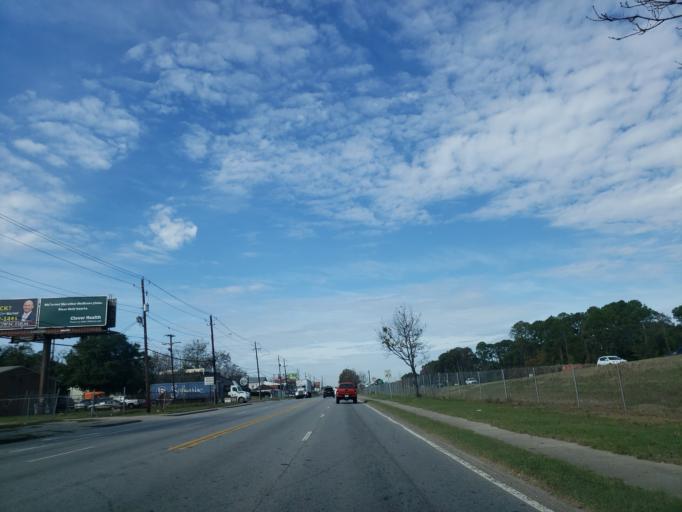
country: US
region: Georgia
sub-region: Chatham County
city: Garden City
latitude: 32.0931
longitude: -81.1335
